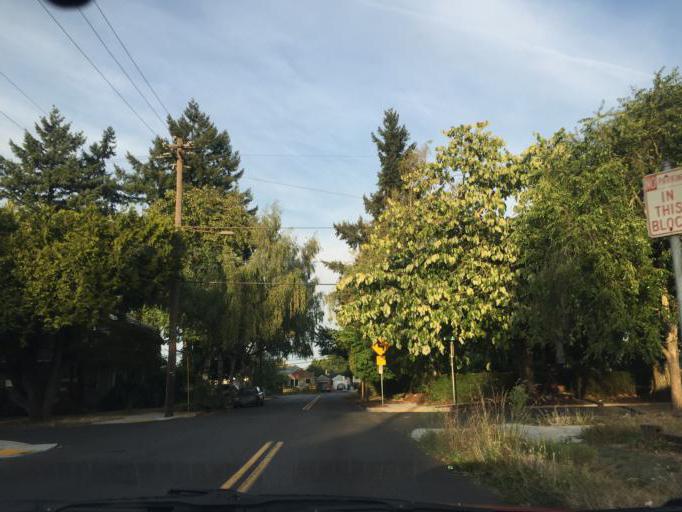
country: US
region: Oregon
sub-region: Multnomah County
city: Portland
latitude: 45.5551
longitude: -122.6270
